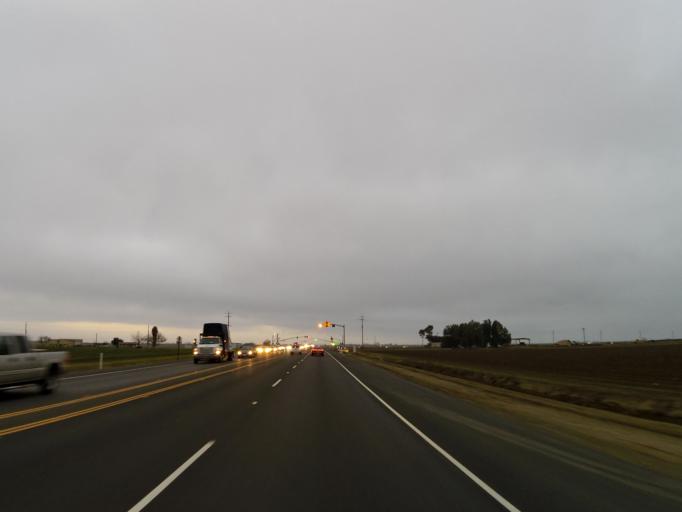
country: US
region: California
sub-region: San Joaquin County
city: Ripon
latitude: 37.6400
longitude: -121.2438
